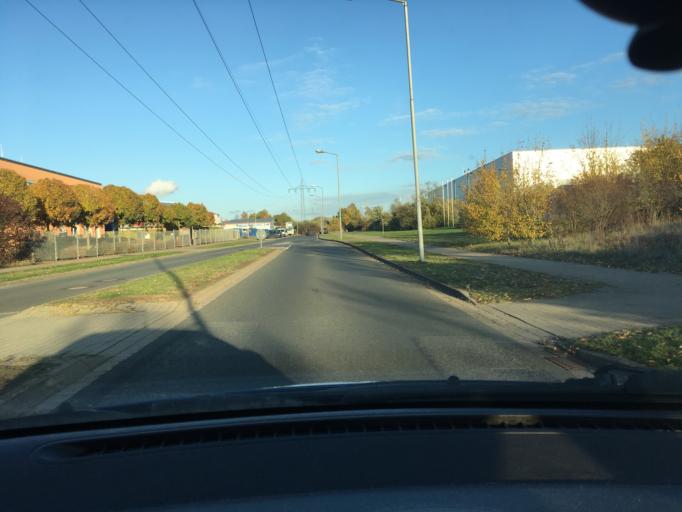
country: DE
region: Lower Saxony
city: Buchholz in der Nordheide
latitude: 53.3532
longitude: 9.8703
